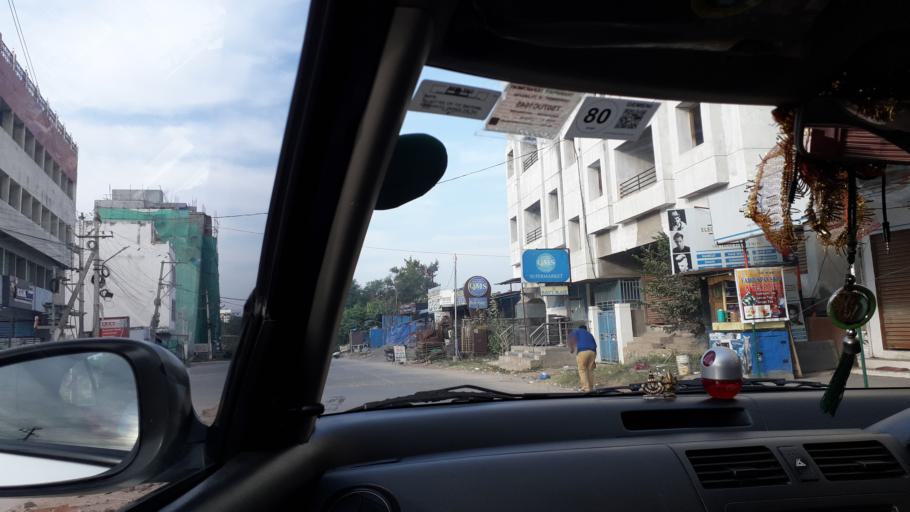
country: IN
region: Telangana
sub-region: Hyderabad
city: Hyderabad
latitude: 17.3945
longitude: 78.3814
